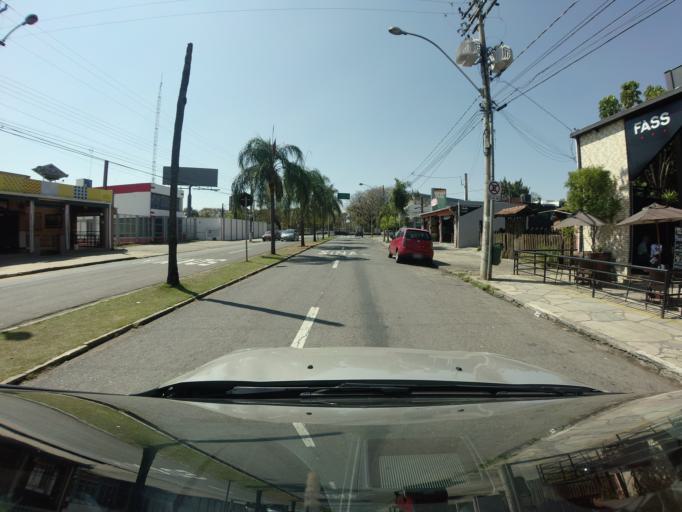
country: BR
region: Sao Paulo
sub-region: Piracicaba
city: Piracicaba
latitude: -22.7129
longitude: -47.6365
